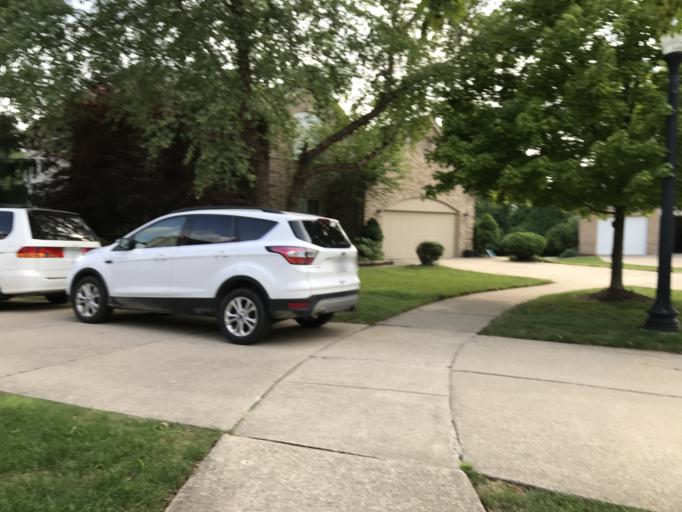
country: US
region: Michigan
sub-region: Oakland County
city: Franklin
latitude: 42.4943
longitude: -83.3346
